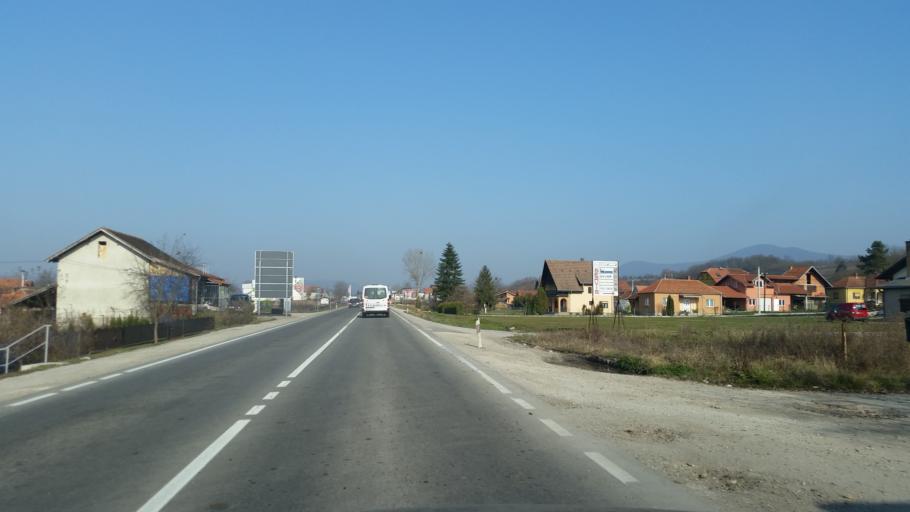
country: RS
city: Prislonica
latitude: 43.9208
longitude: 20.4086
